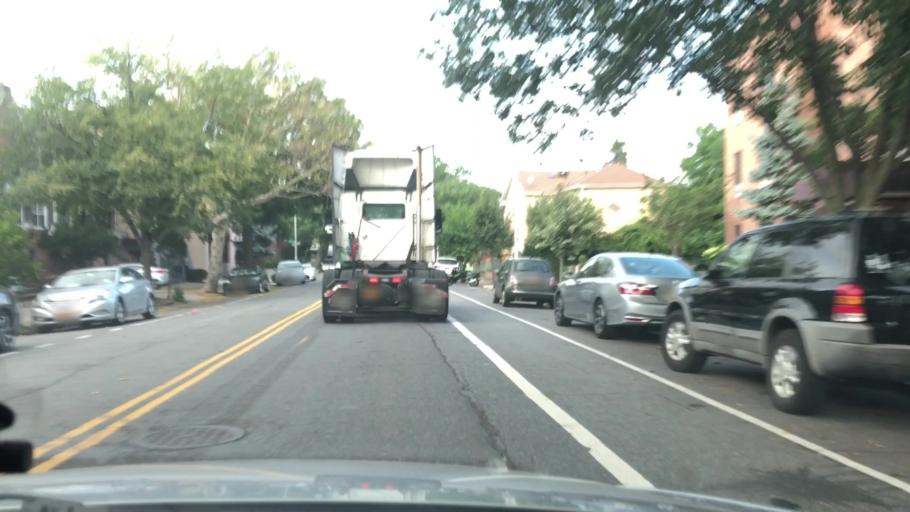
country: US
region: New York
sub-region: Kings County
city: Brooklyn
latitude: 40.6536
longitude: -73.9810
